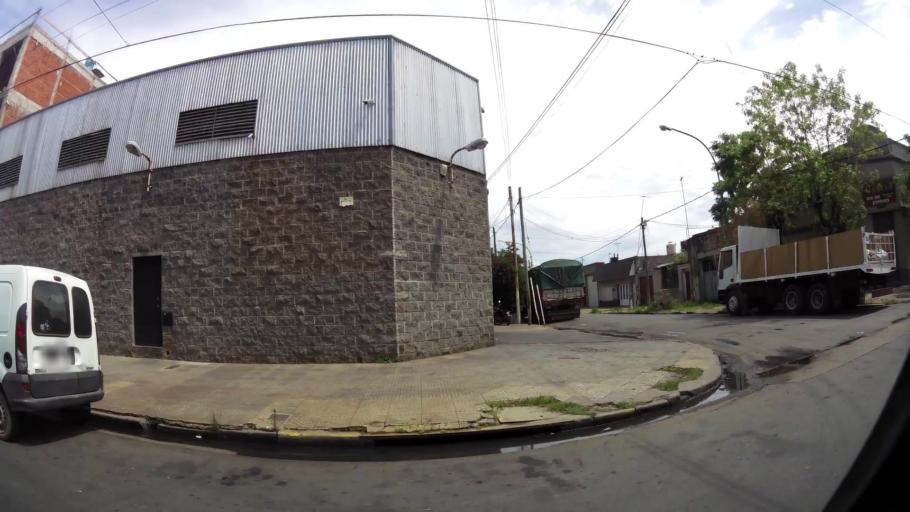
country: AR
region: Buenos Aires
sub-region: Partido de Avellaneda
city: Avellaneda
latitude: -34.6698
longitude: -58.3985
